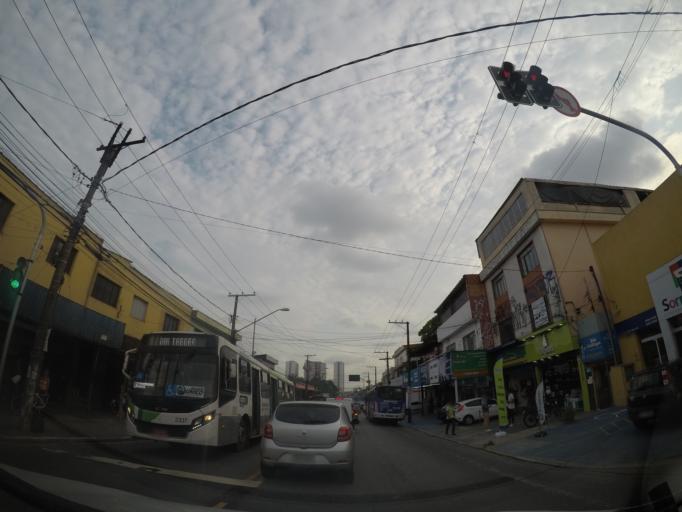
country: BR
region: Sao Paulo
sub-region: Guarulhos
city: Guarulhos
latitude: -23.4495
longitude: -46.5084
